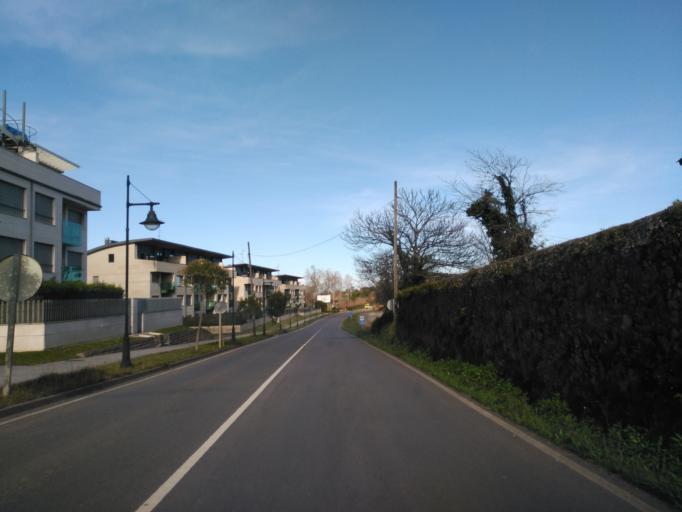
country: ES
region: Asturias
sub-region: Province of Asturias
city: Llanes
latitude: 43.4080
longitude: -4.7580
